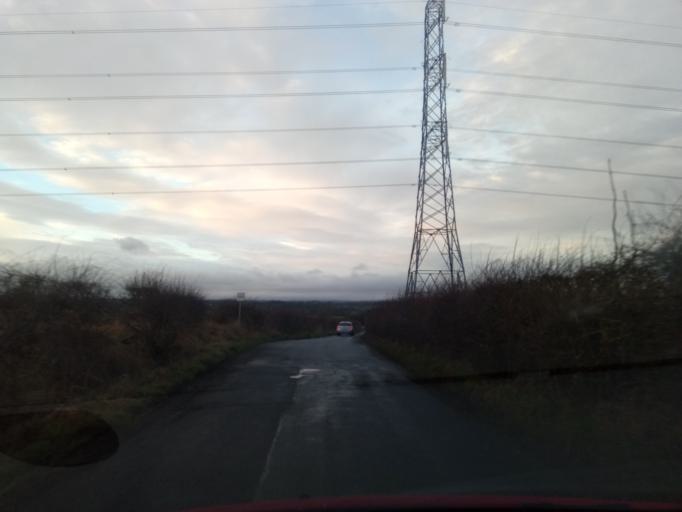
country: GB
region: England
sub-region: Northumberland
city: Ponteland
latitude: 55.0787
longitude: -1.7371
